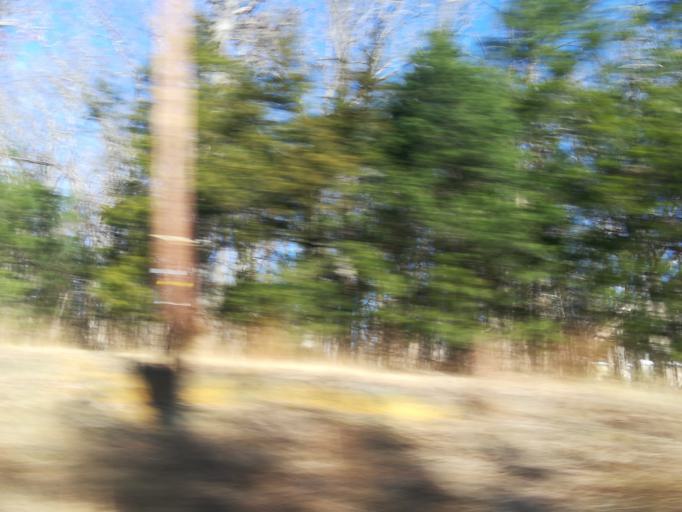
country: US
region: North Carolina
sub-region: Durham County
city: Durham
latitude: 36.0331
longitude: -78.9930
